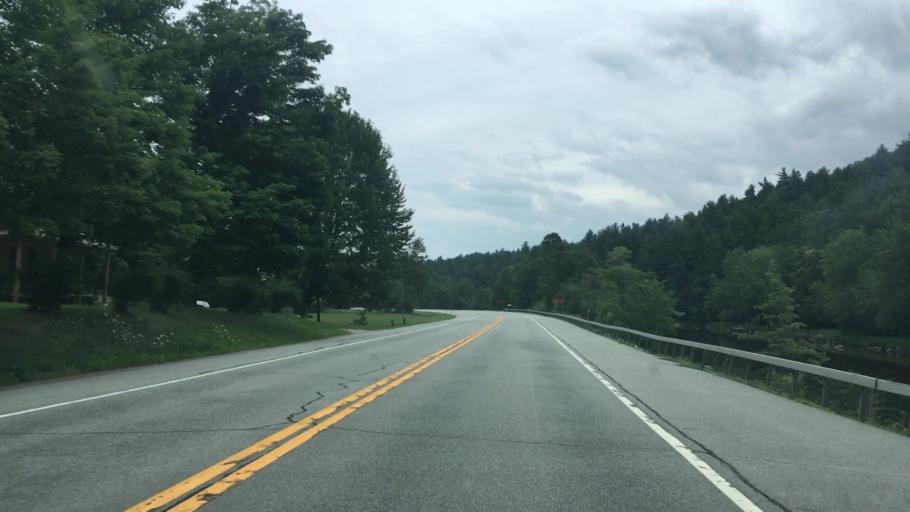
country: US
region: New York
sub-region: Essex County
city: Elizabethtown
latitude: 44.3465
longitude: -73.7620
